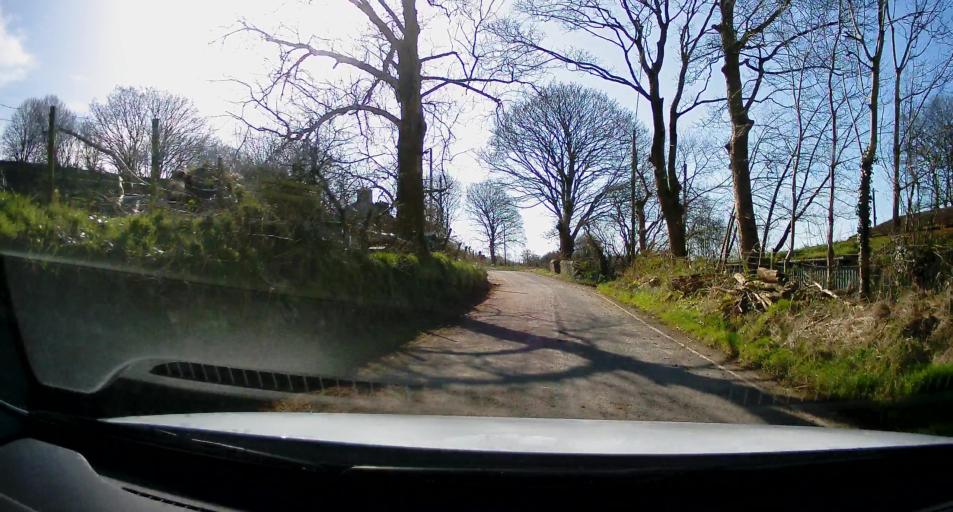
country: GB
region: Wales
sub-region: County of Ceredigion
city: Lledrod
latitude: 52.2755
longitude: -4.0658
